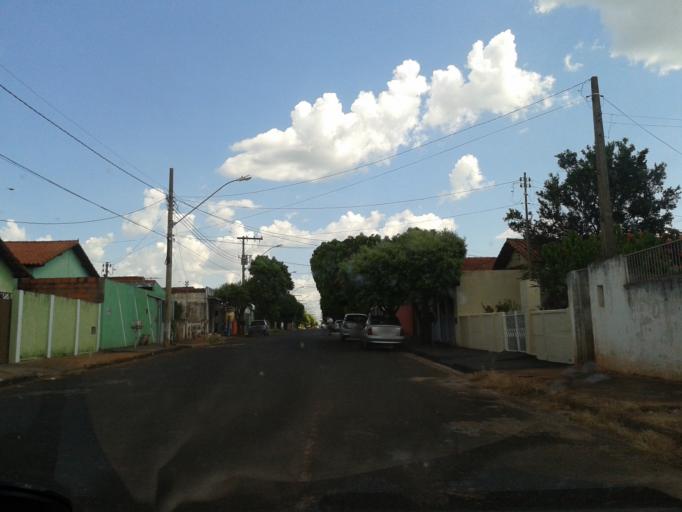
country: BR
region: Minas Gerais
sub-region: Ituiutaba
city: Ituiutaba
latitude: -18.9834
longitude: -49.4497
